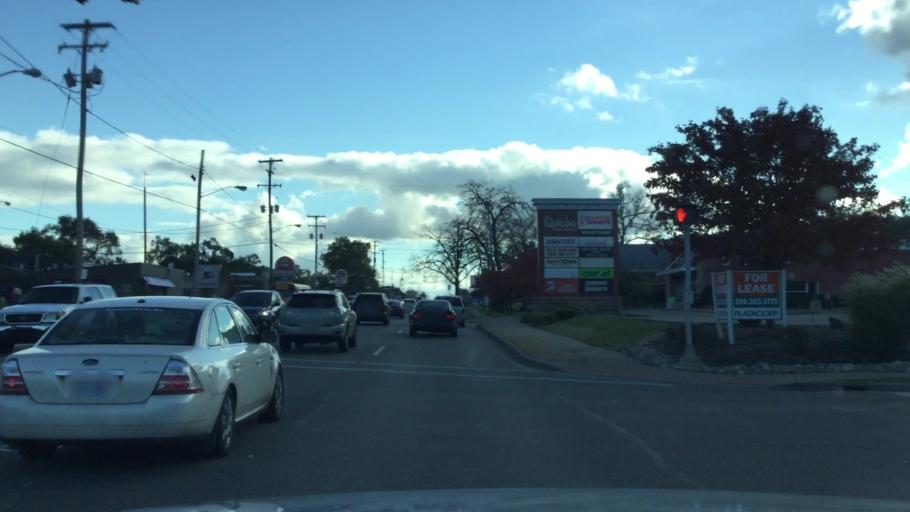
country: US
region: Michigan
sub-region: Kalamazoo County
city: Kalamazoo
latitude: 42.2604
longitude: -85.5897
